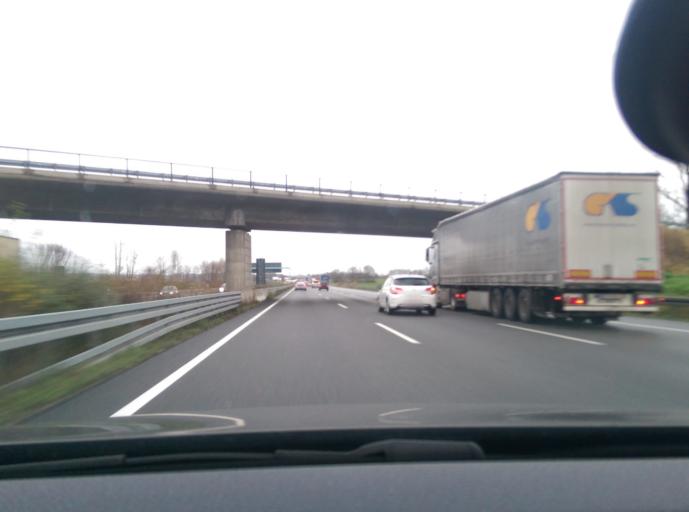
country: DE
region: Lower Saxony
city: Rosdorf
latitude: 51.4682
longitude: 9.8713
